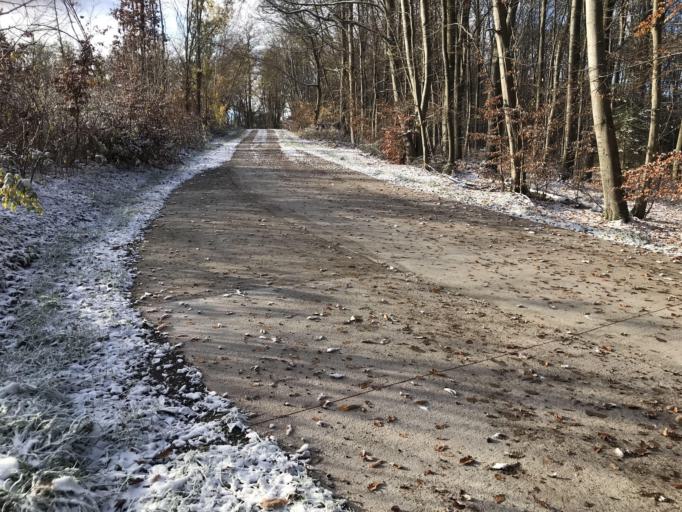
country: DE
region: Saxony-Anhalt
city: Harzgerode
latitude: 51.6025
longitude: 11.1280
